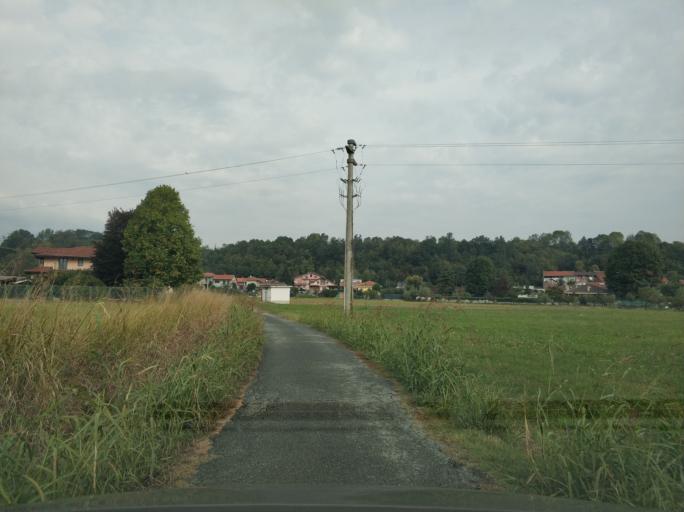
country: IT
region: Piedmont
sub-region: Provincia di Torino
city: Nole
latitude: 45.2543
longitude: 7.5730
